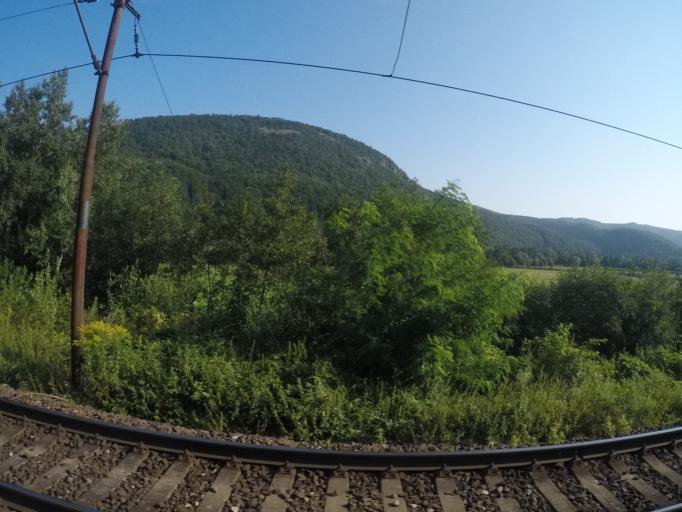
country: SK
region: Presovsky
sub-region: Okres Presov
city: Presov
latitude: 48.8513
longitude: 21.1725
